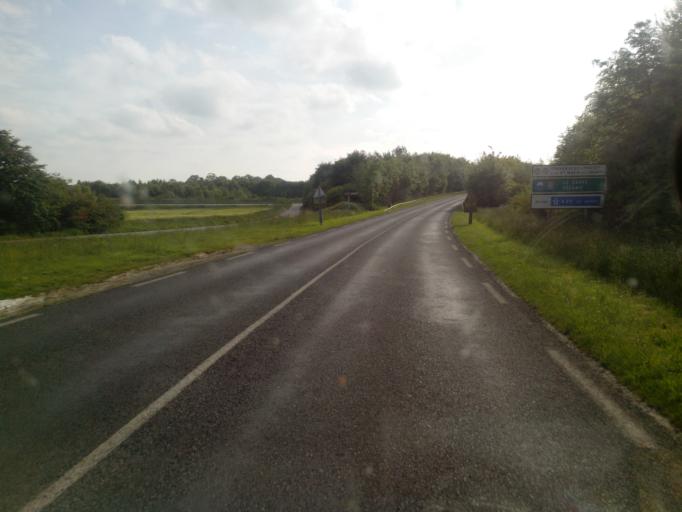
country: FR
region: Haute-Normandie
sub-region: Departement de la Seine-Maritime
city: Sainte-Marie-des-Champs
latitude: 49.6324
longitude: 0.8105
